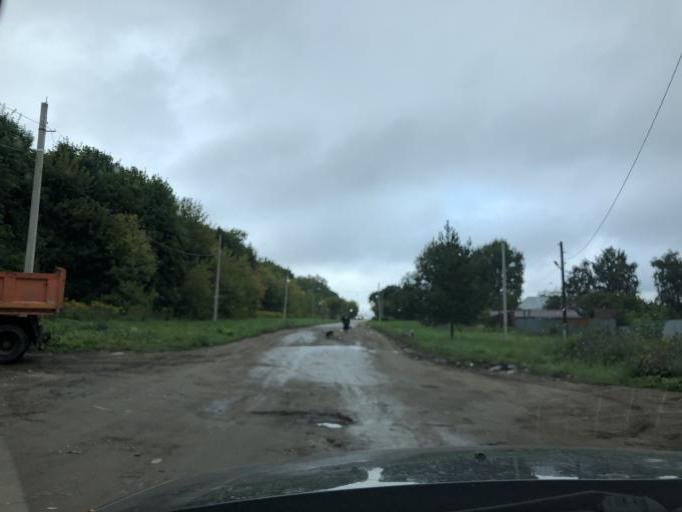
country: RU
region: Tula
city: Mendeleyevskiy
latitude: 54.1746
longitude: 37.5518
